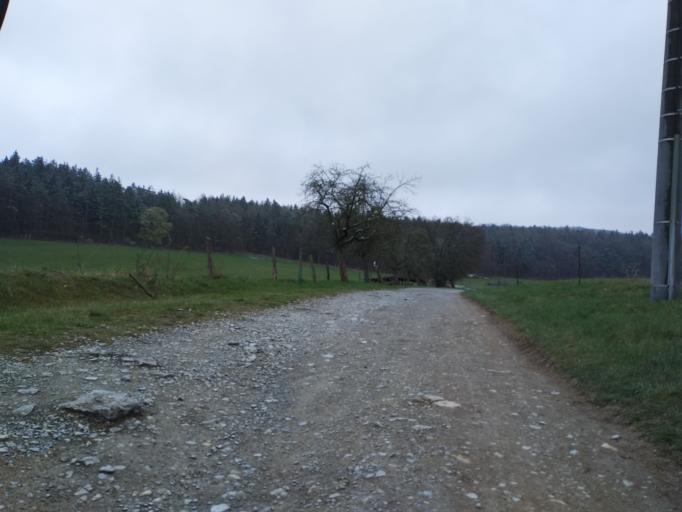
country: DE
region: Thuringia
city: Buchfart
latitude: 50.9178
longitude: 11.3327
